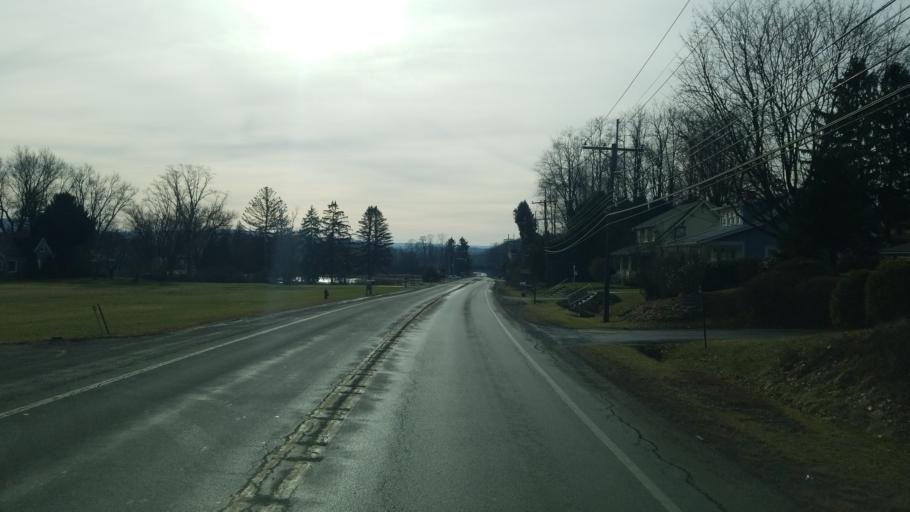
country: US
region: Pennsylvania
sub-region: Indiana County
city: Indiana
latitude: 40.6031
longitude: -79.1471
